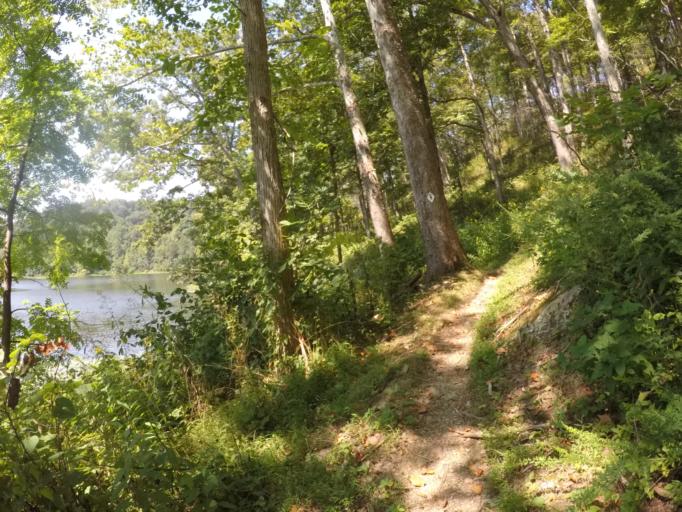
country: US
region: Ohio
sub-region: Lawrence County
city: Ironton
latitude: 38.6197
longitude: -82.6258
